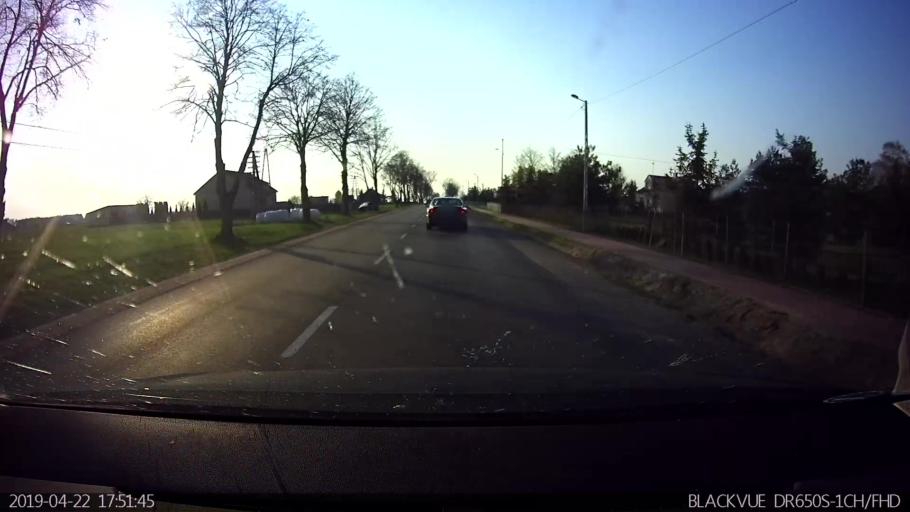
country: PL
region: Masovian Voivodeship
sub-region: Powiat wegrowski
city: Wegrow
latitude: 52.4367
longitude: 21.9901
